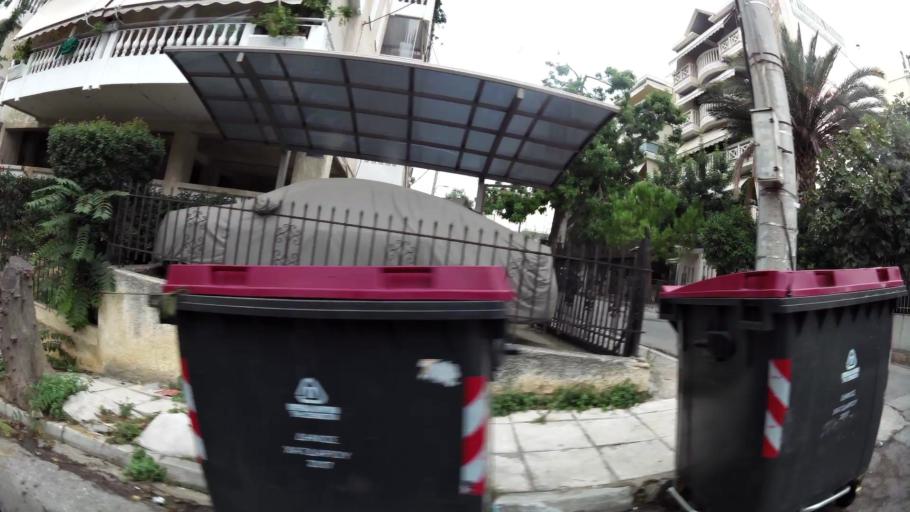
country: GR
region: Attica
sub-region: Nomarchia Athinas
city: Chaidari
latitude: 38.0067
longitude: 23.6686
